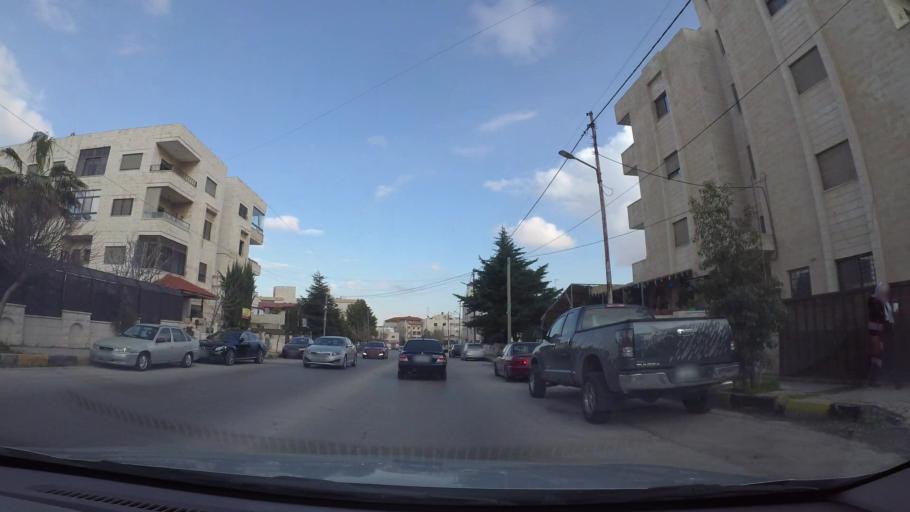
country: JO
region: Amman
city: Wadi as Sir
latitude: 31.9788
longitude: 35.8518
